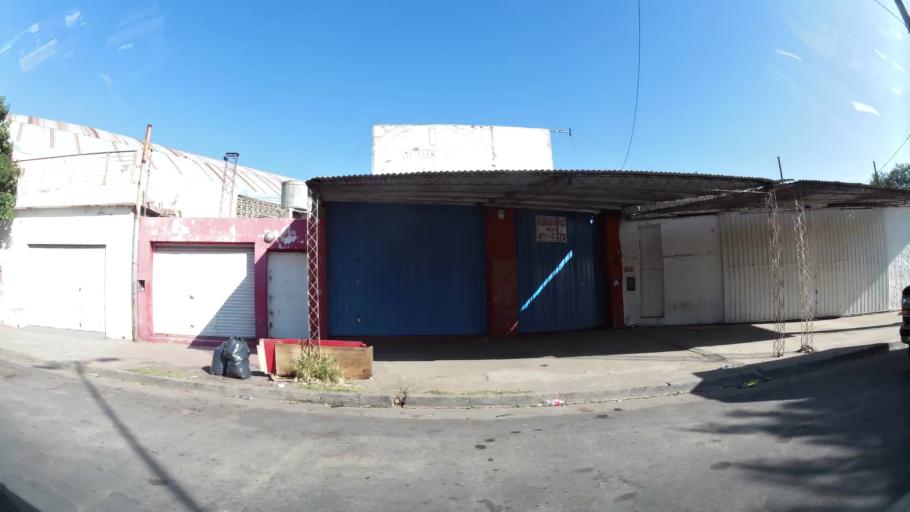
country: AR
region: Cordoba
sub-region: Departamento de Capital
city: Cordoba
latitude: -31.4756
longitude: -64.2229
